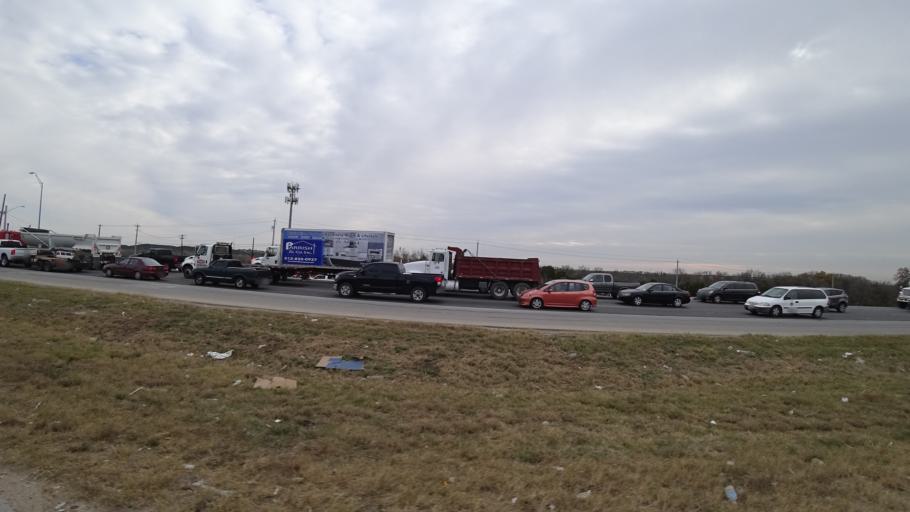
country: US
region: Texas
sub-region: Travis County
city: Austin
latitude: 30.3022
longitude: -97.6611
